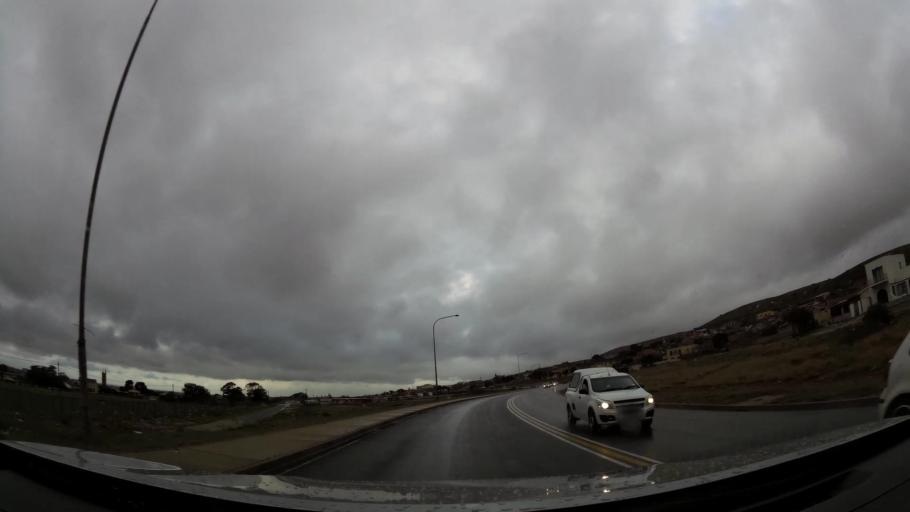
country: ZA
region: Eastern Cape
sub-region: Nelson Mandela Bay Metropolitan Municipality
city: Port Elizabeth
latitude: -33.8889
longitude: 25.5191
